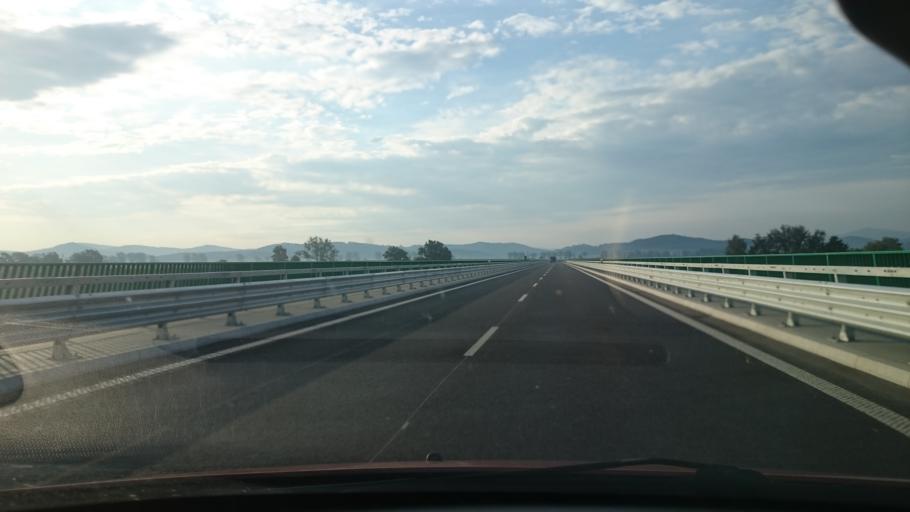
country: PL
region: Lower Silesian Voivodeship
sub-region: Powiat klodzki
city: Klodzko
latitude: 50.4037
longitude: 16.6422
